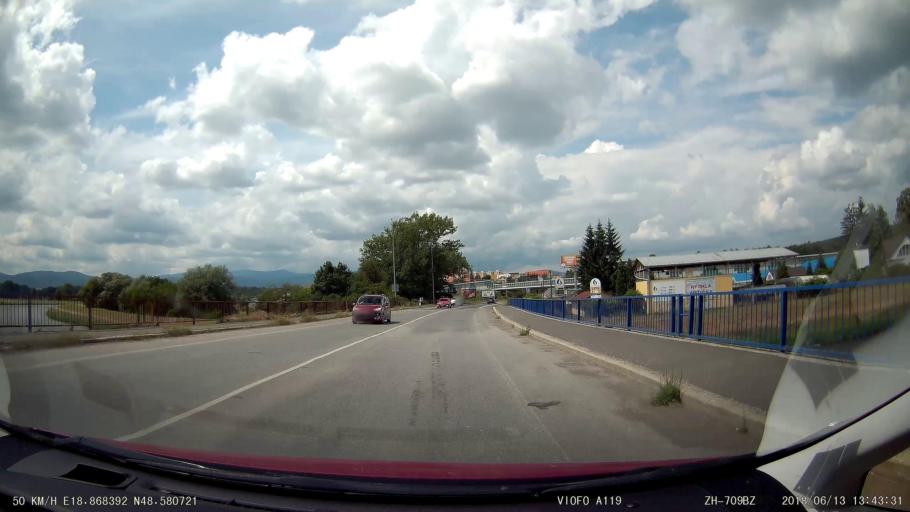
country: SK
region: Banskobystricky
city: Ziar nad Hronom
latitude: 48.5809
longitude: 18.8680
